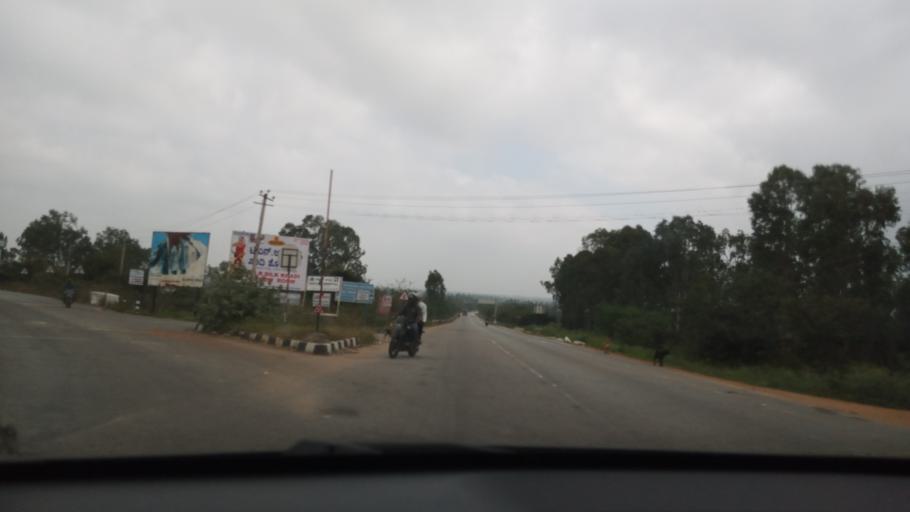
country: IN
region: Karnataka
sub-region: Chikkaballapur
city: Chintamani
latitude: 13.3605
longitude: 78.0407
